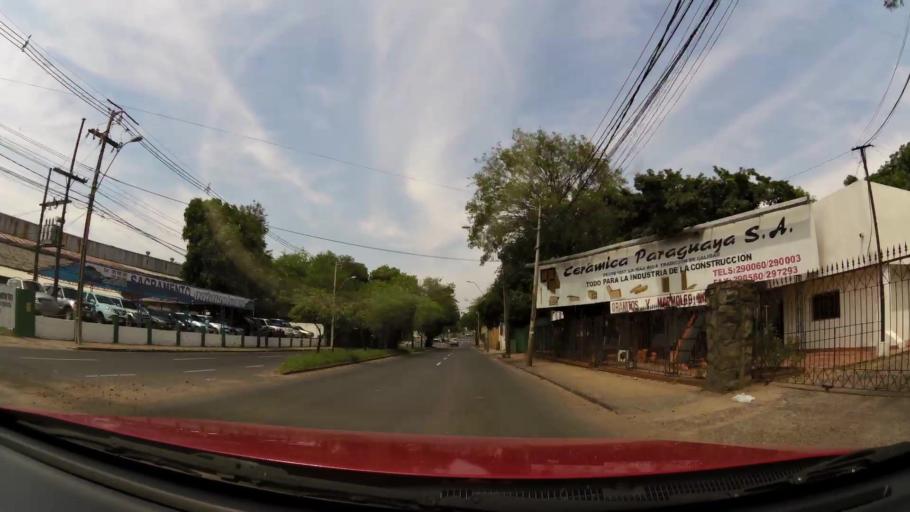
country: PY
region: Asuncion
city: Asuncion
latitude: -25.2619
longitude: -57.5814
